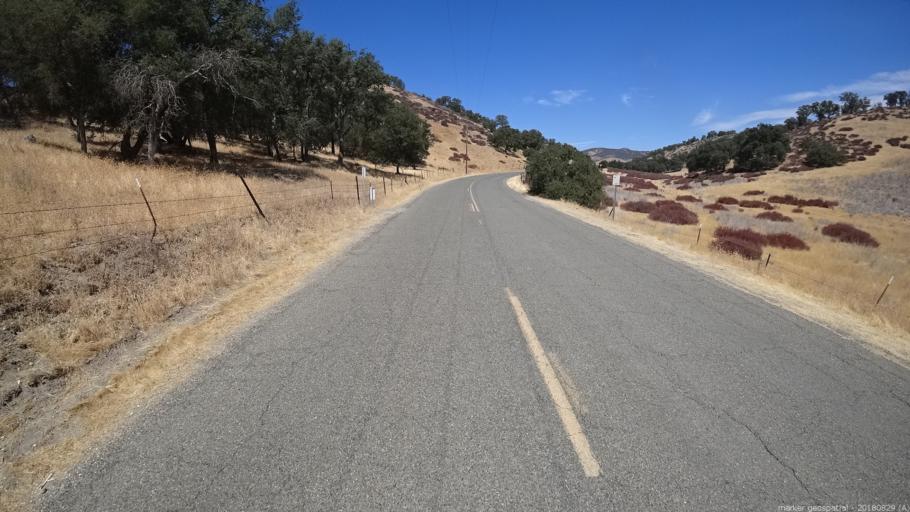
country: US
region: California
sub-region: San Luis Obispo County
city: Lake Nacimiento
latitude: 35.8840
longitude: -120.9925
